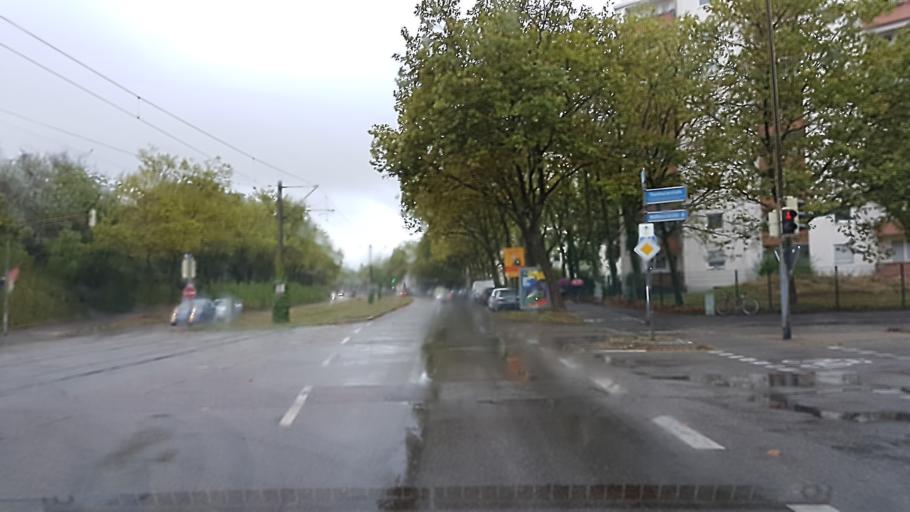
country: DE
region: Baden-Wuerttemberg
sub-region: Freiburg Region
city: Freiburg
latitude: 48.0081
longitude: 7.8157
